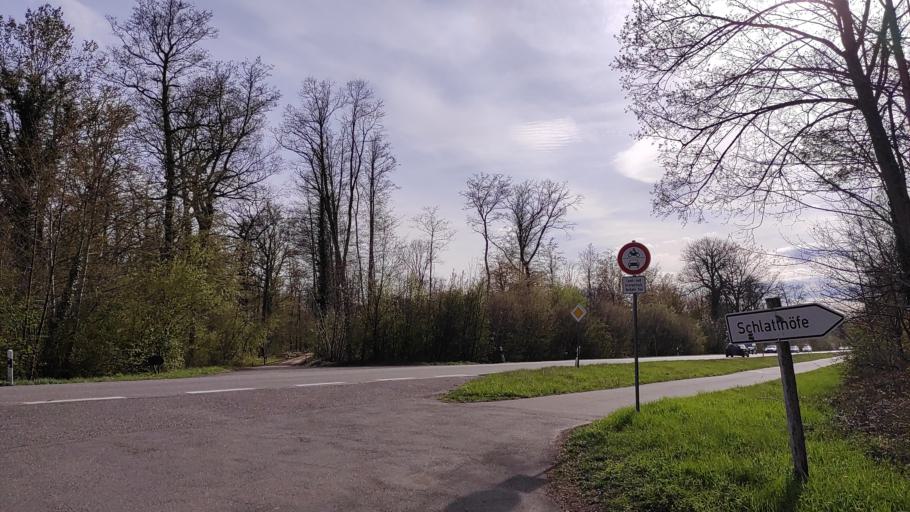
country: DE
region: Baden-Wuerttemberg
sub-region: Freiburg Region
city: Schallstadt
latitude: 47.9809
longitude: 7.7569
